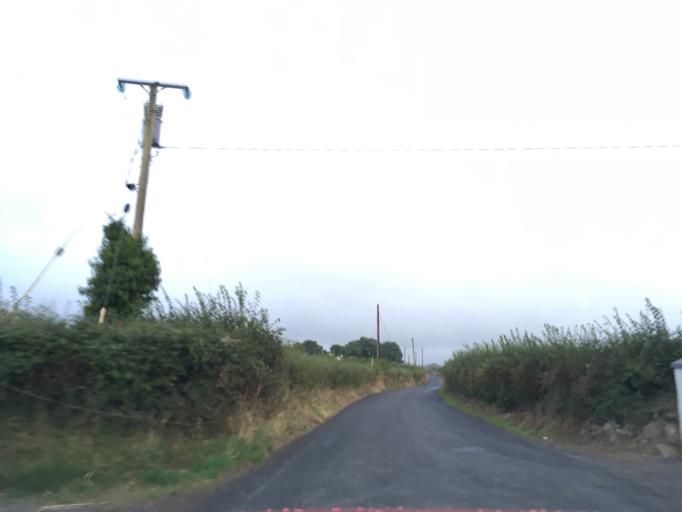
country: IE
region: Munster
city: Cashel
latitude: 52.4663
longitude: -7.9760
